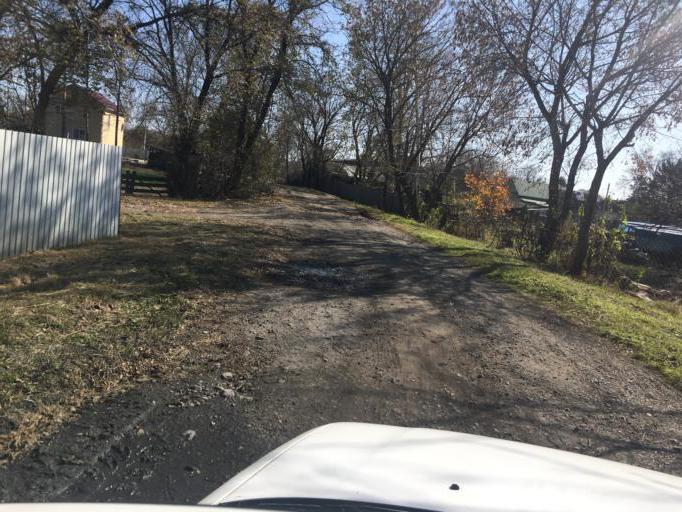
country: RU
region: Primorskiy
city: Dal'nerechensk
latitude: 45.9103
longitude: 133.7937
